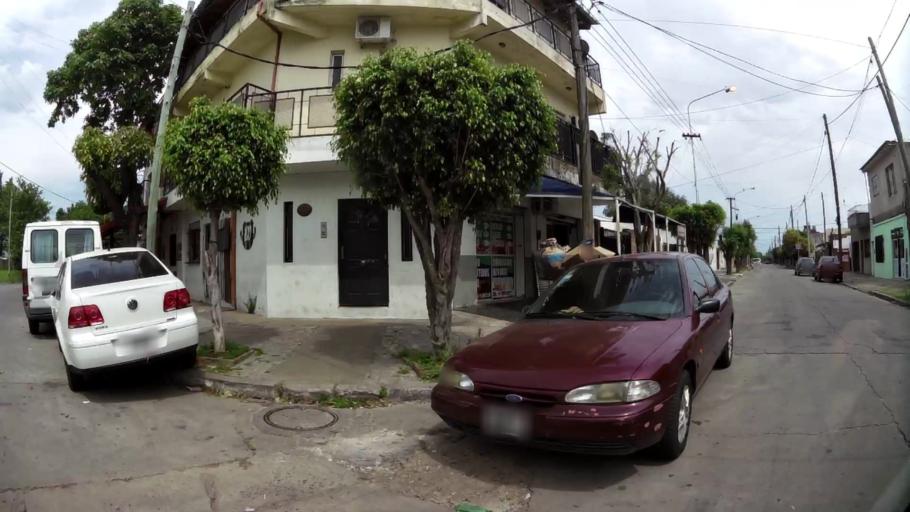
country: AR
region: Buenos Aires F.D.
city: Villa Lugano
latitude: -34.6871
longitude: -58.5012
